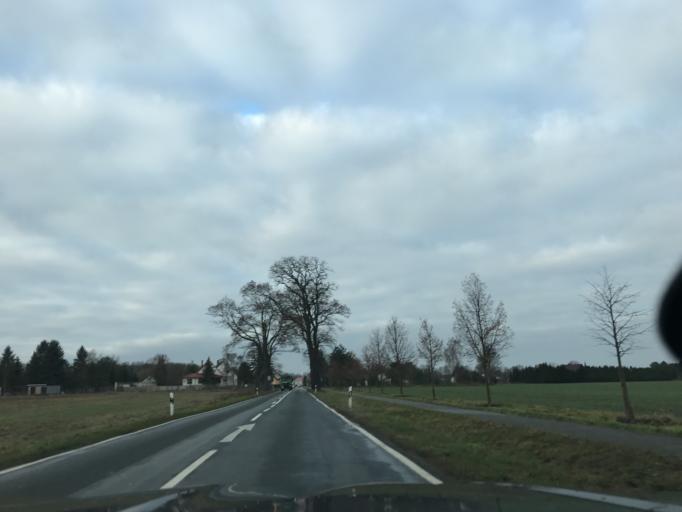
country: DE
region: Brandenburg
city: Golzow
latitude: 52.3405
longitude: 12.6920
